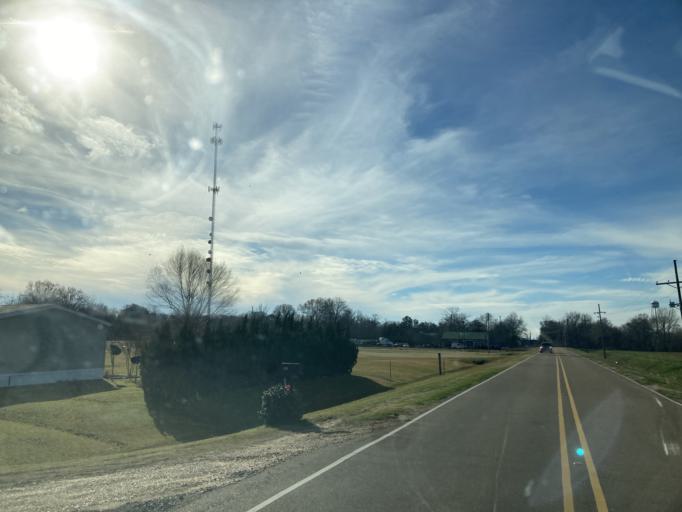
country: US
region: Mississippi
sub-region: Humphreys County
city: Belzoni
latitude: 32.9886
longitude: -90.5901
